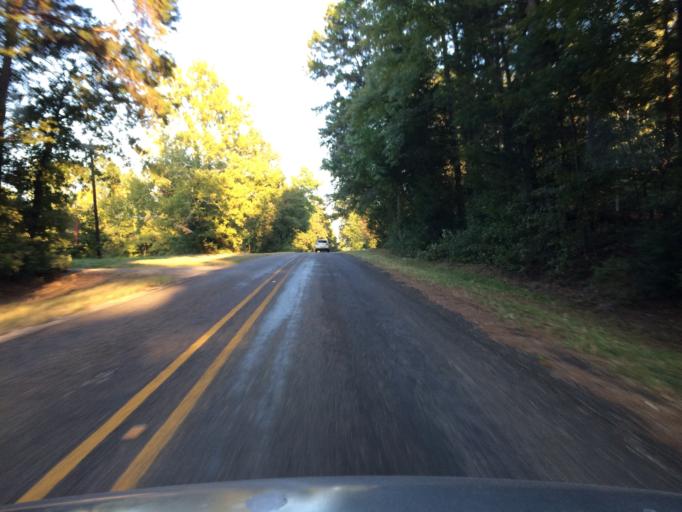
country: US
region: Texas
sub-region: Wood County
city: Hawkins
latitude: 32.7344
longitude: -95.2419
